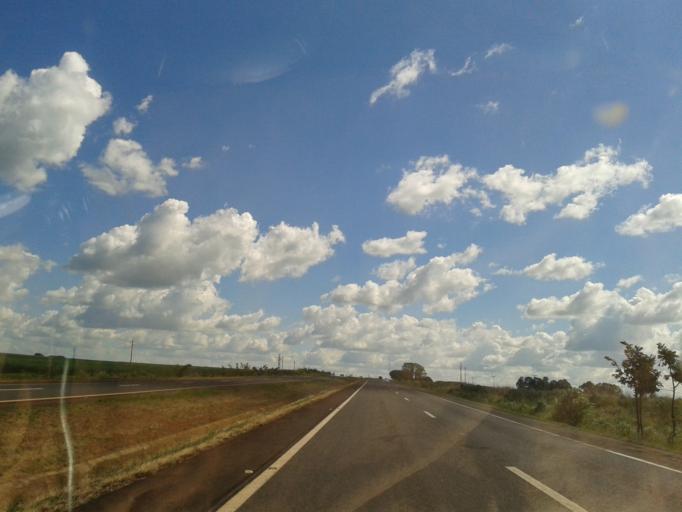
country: BR
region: Goias
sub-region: Morrinhos
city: Morrinhos
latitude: -17.8306
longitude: -49.2148
